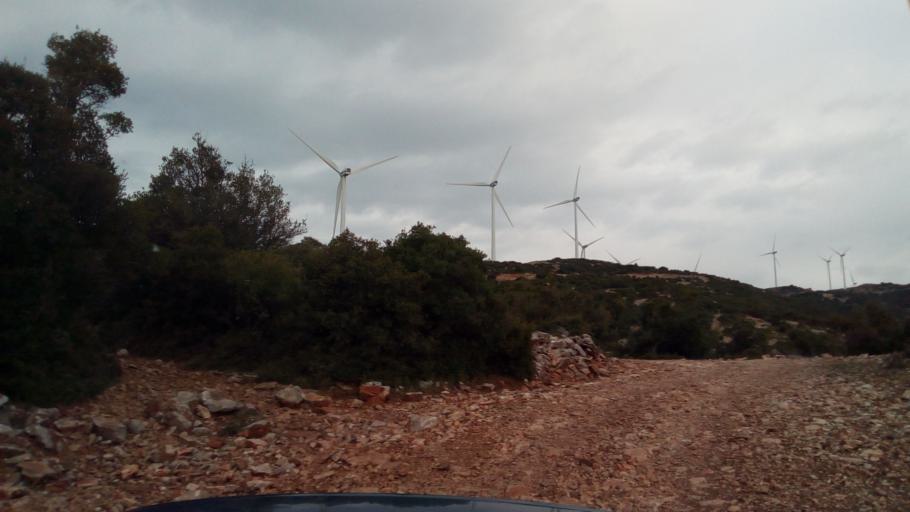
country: GR
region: West Greece
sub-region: Nomos Achaias
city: Kamarai
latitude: 38.4123
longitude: 22.0425
